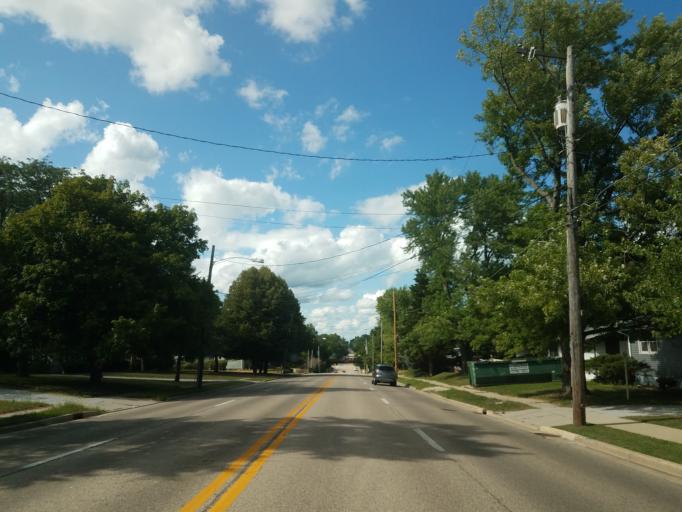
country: US
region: Illinois
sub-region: McLean County
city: Normal
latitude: 40.5003
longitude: -88.9821
